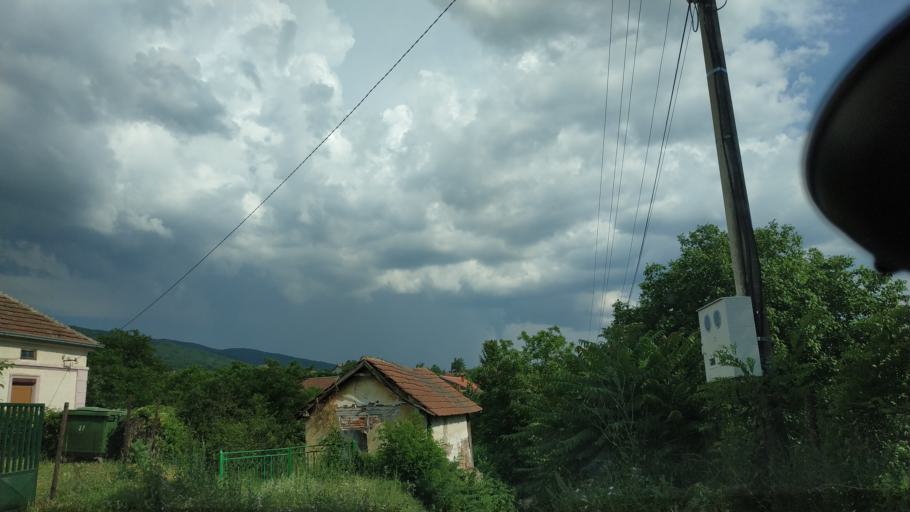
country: RS
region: Central Serbia
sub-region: Nisavski Okrug
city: Aleksinac
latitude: 43.6019
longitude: 21.6899
